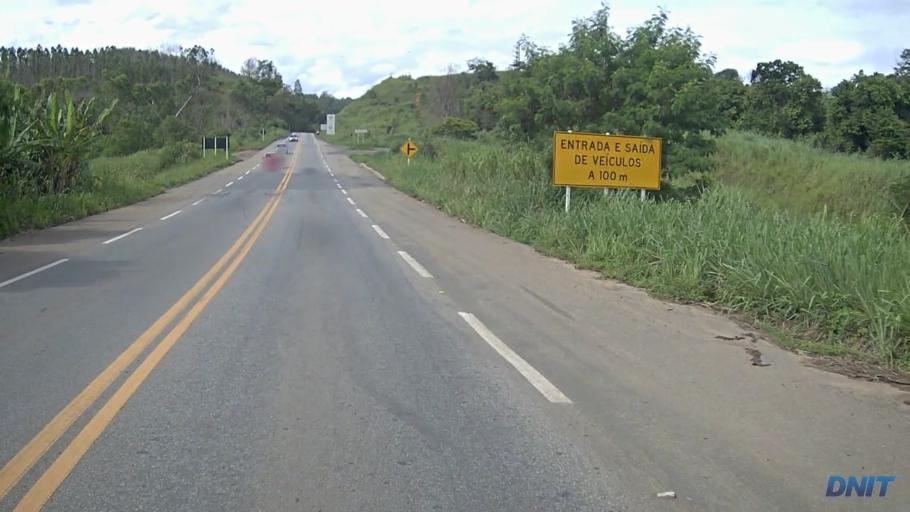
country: BR
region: Minas Gerais
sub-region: Ipaba
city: Ipaba
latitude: -19.3367
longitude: -42.4255
